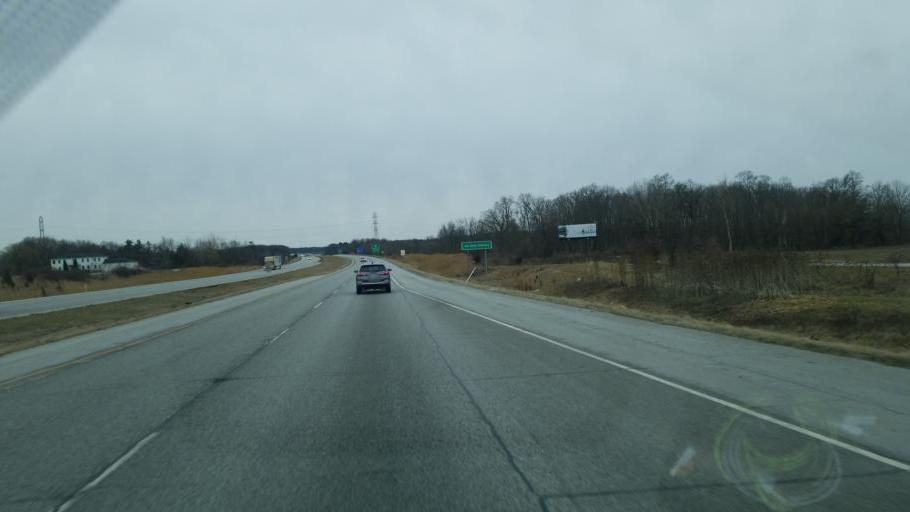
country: US
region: Indiana
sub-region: Porter County
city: Chesterton
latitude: 41.5714
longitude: -87.0464
